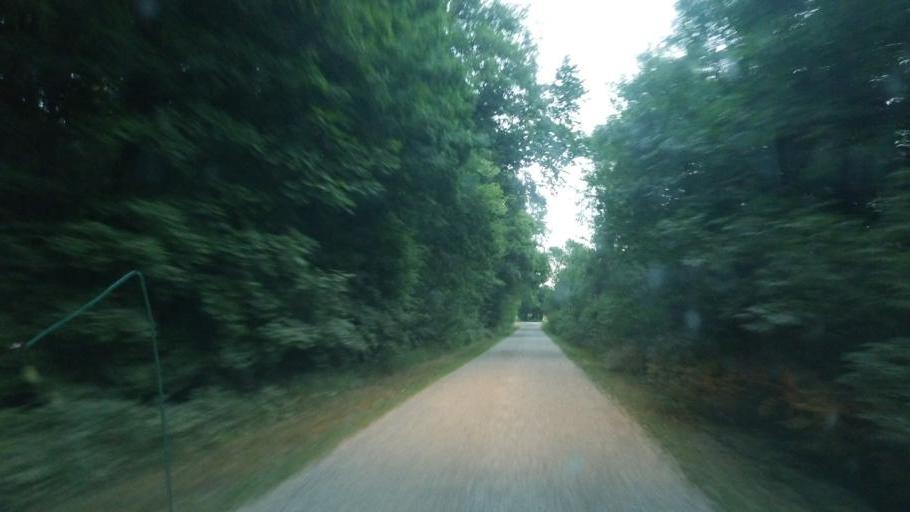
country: US
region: Ohio
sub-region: Defiance County
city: Hicksville
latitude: 41.3663
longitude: -84.8040
